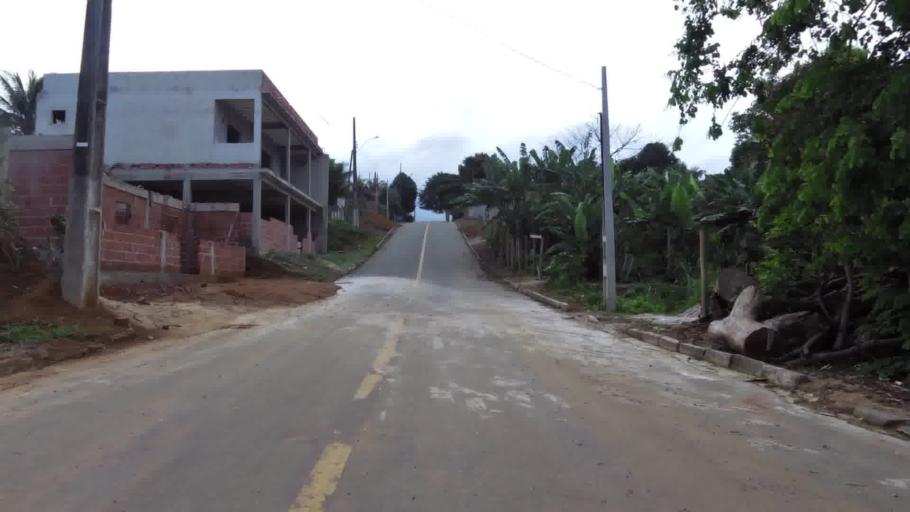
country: BR
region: Espirito Santo
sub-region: Piuma
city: Piuma
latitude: -20.7935
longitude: -40.6412
